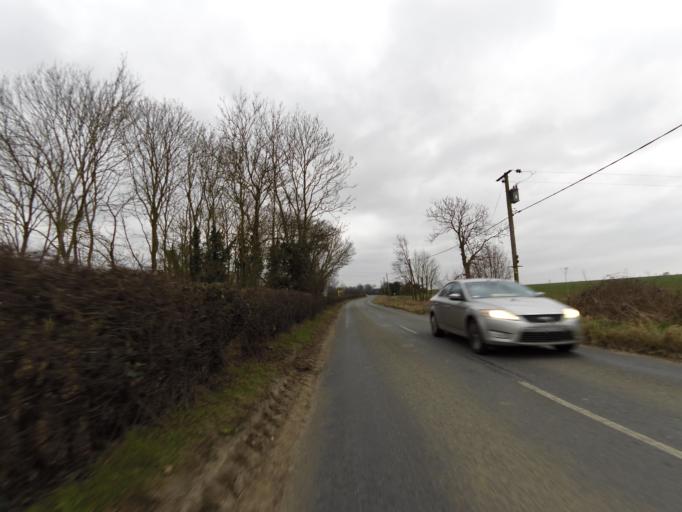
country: GB
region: England
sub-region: Suffolk
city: Ipswich
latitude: 52.1269
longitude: 1.1454
